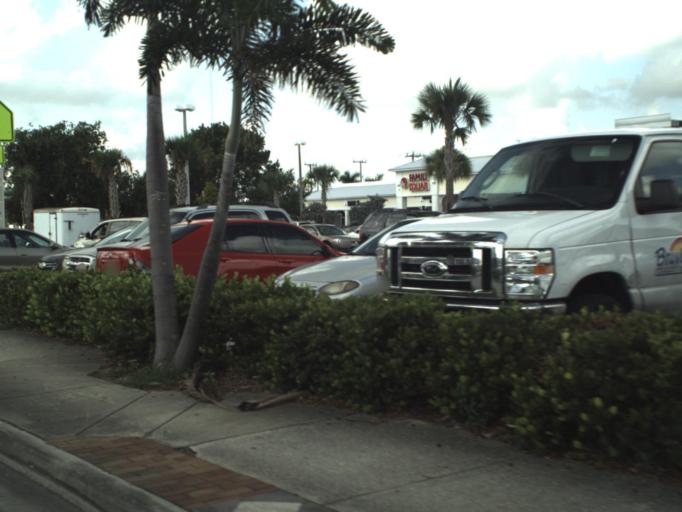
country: US
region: Florida
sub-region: Broward County
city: Lauderhill
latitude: 26.1475
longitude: -80.2029
